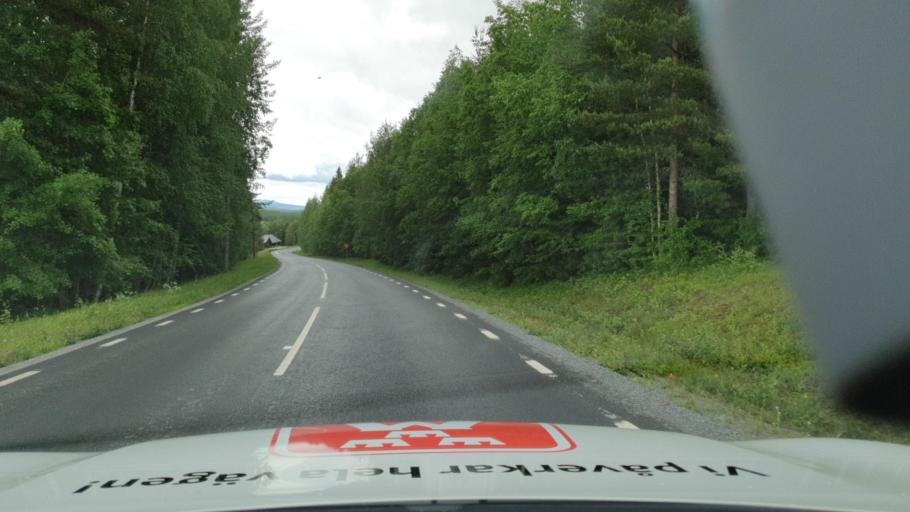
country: SE
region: Vaesterbotten
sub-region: Dorotea Kommun
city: Dorotea
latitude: 64.2383
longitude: 16.5407
